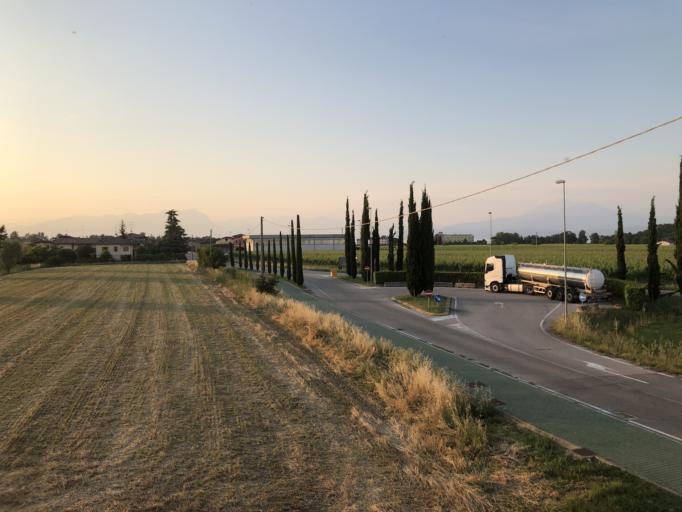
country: IT
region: Lombardy
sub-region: Provincia di Brescia
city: San Martino della Battaglia
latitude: 45.4495
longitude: 10.6420
